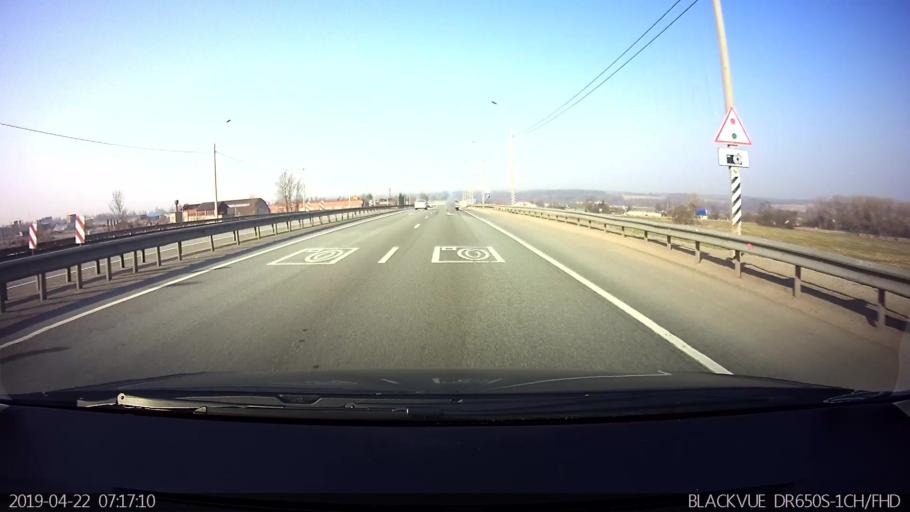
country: RU
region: Smolensk
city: Vyaz'ma
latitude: 55.2445
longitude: 34.3182
